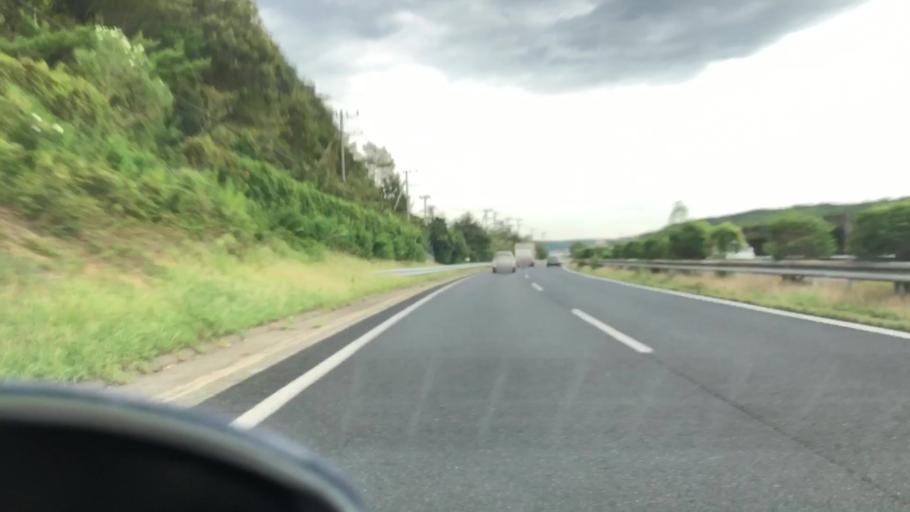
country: JP
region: Hyogo
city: Yashiro
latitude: 34.9199
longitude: 135.0044
